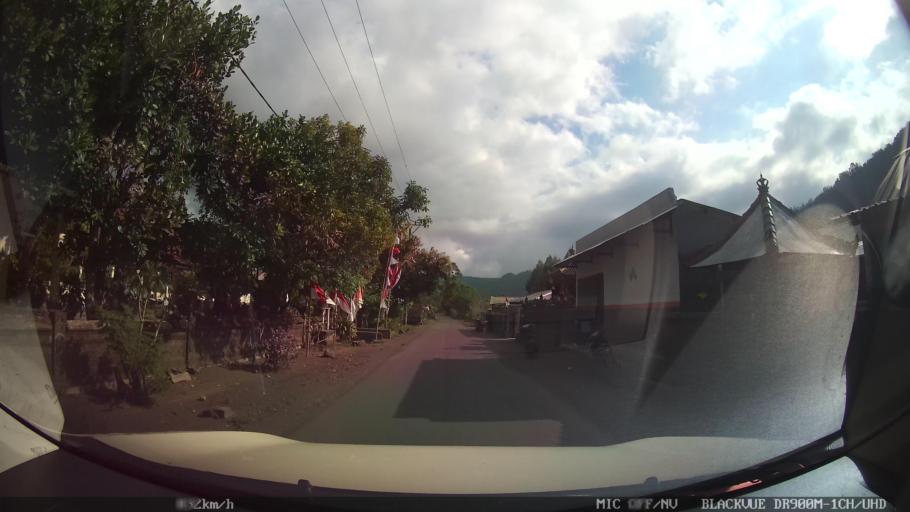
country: ID
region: Bali
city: Banjar Kedisan
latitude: -8.2205
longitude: 115.3629
